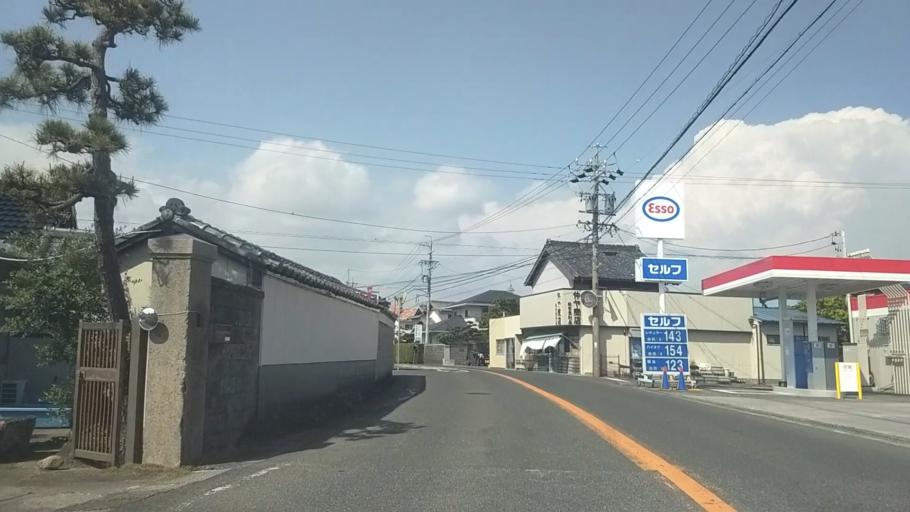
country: JP
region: Shizuoka
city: Hamamatsu
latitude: 34.6803
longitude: 137.7093
